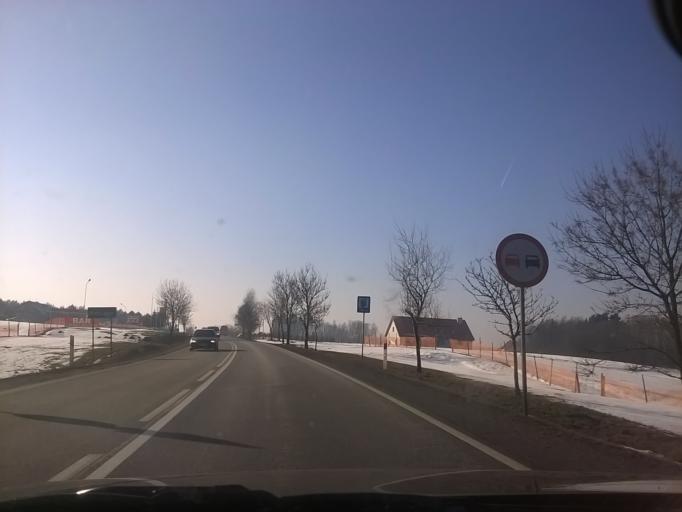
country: PL
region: Warmian-Masurian Voivodeship
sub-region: Powiat mragowski
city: Mragowo
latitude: 53.8452
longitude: 21.2236
